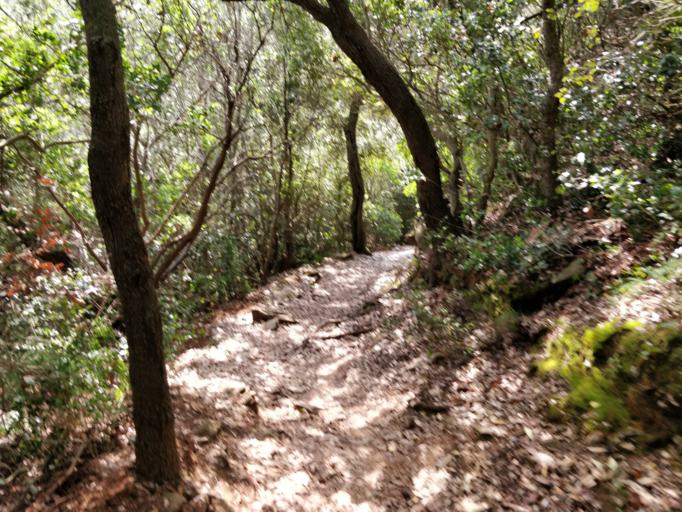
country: FR
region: Provence-Alpes-Cote d'Azur
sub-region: Departement du Var
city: Le Lavandou
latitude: 43.0109
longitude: 6.3899
